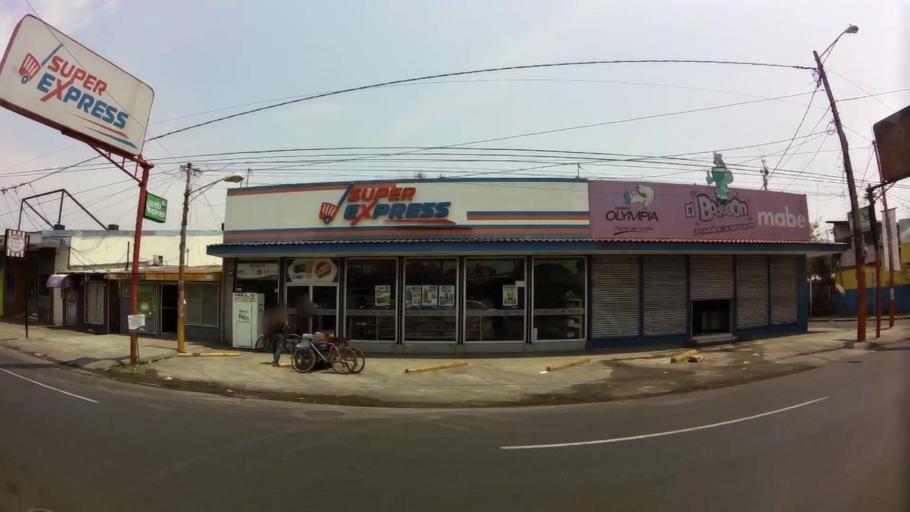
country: NI
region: Managua
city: Ciudad Sandino
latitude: 12.1521
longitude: -86.3071
